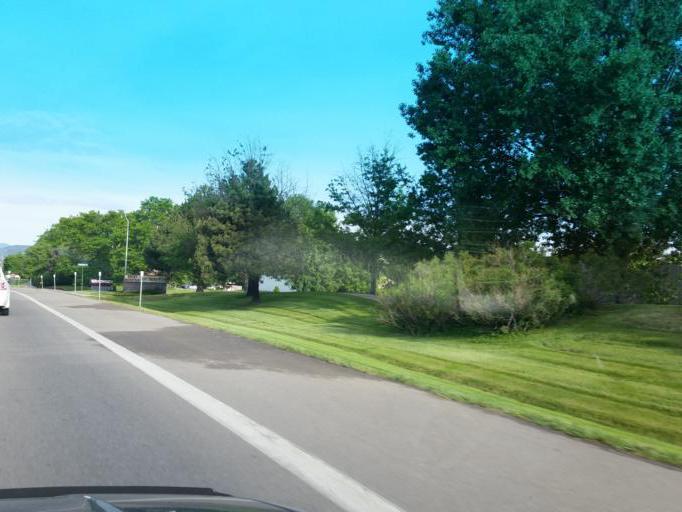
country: US
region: Colorado
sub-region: Larimer County
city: Fort Collins
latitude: 40.5237
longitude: -105.0451
